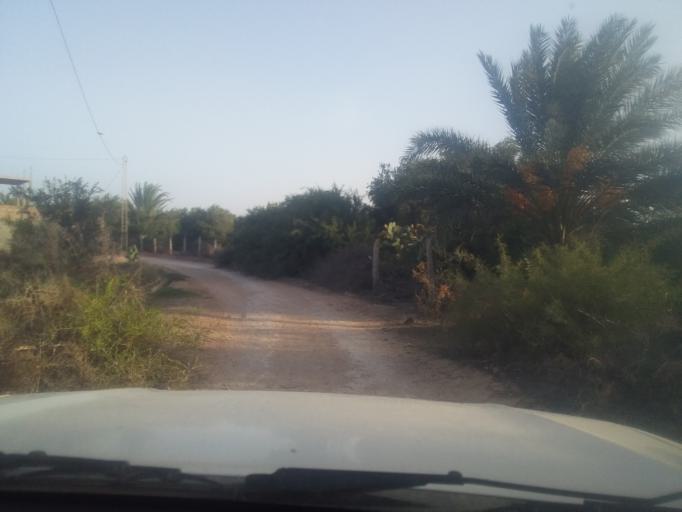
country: TN
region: Qabis
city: Gabes
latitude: 33.6305
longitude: 10.2950
